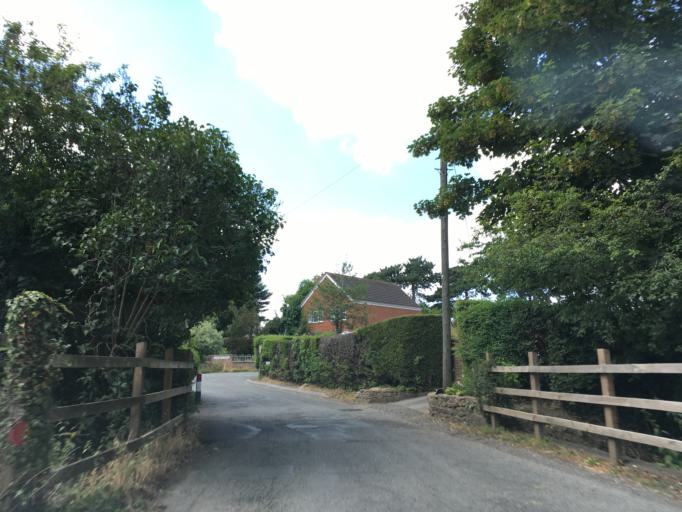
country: GB
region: England
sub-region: Gloucestershire
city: Barnwood
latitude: 51.8332
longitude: -2.1923
